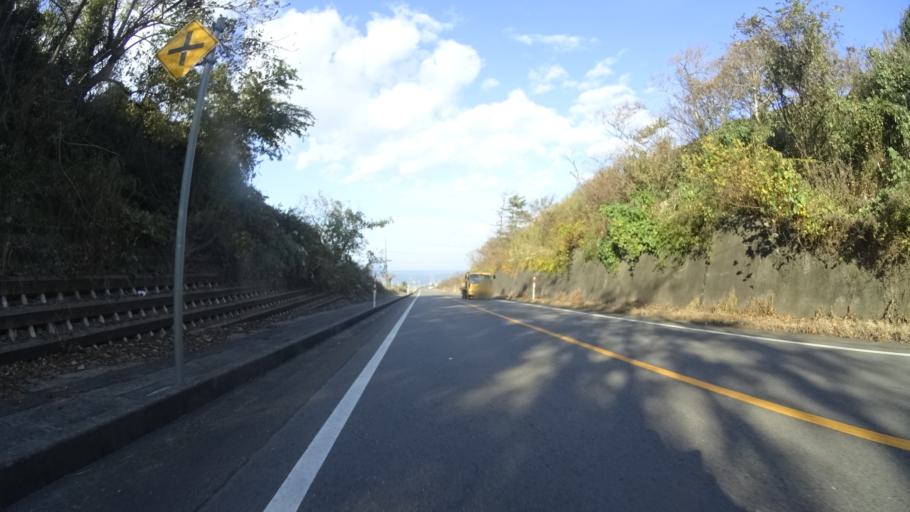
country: JP
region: Niigata
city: Kashiwazaki
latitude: 37.2882
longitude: 138.4003
